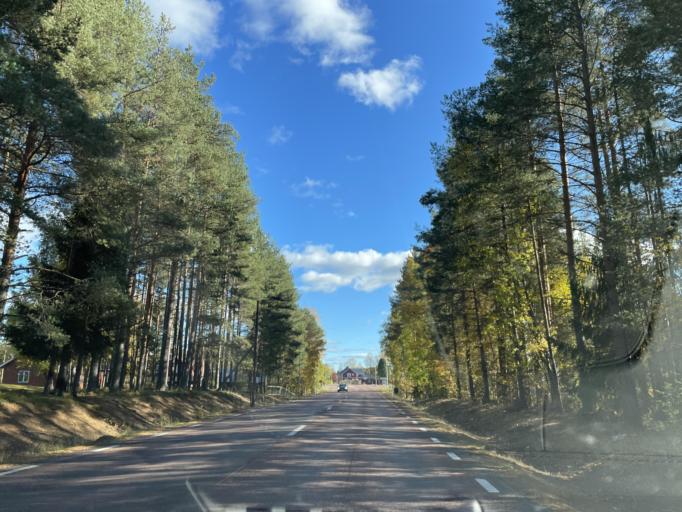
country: SE
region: Dalarna
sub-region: Malung-Saelens kommun
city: Malung
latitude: 60.7358
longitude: 13.5550
